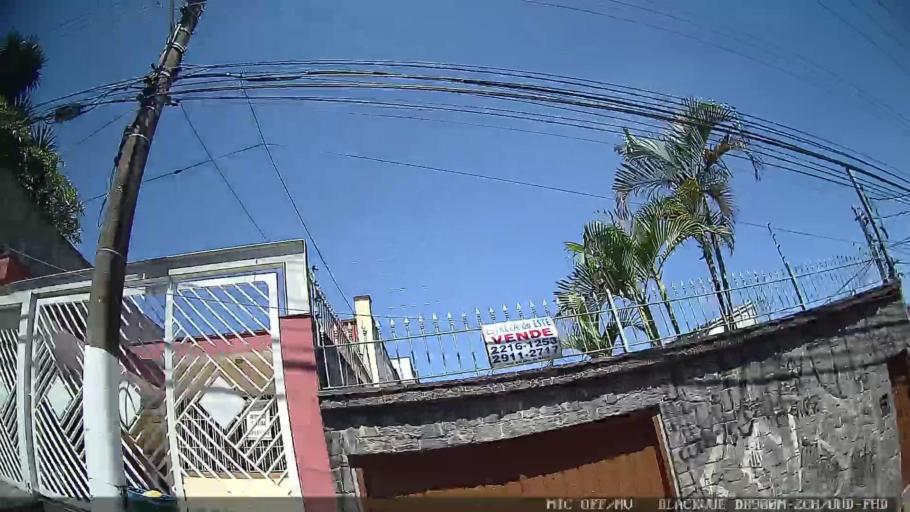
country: BR
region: Sao Paulo
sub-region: Sao Caetano Do Sul
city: Sao Caetano do Sul
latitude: -23.5910
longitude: -46.5337
